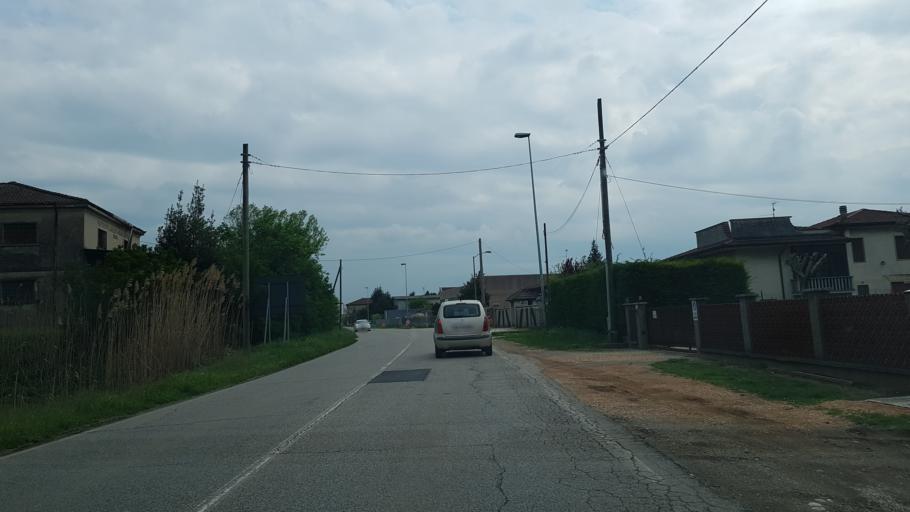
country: IT
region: Veneto
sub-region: Provincia di Verona
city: Maccacari
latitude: 45.1493
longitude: 11.1341
